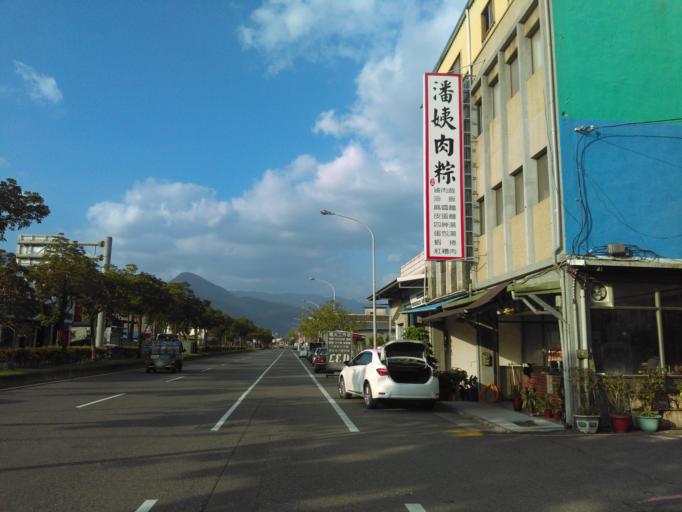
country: TW
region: Taiwan
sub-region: Yilan
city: Yilan
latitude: 24.7987
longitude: 121.7644
